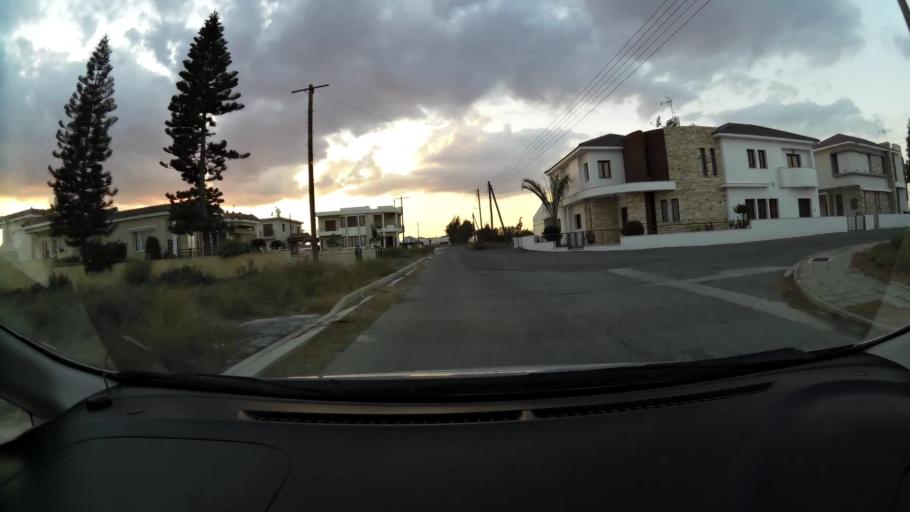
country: CY
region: Larnaka
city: Dhromolaxia
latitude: 34.8786
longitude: 33.5829
